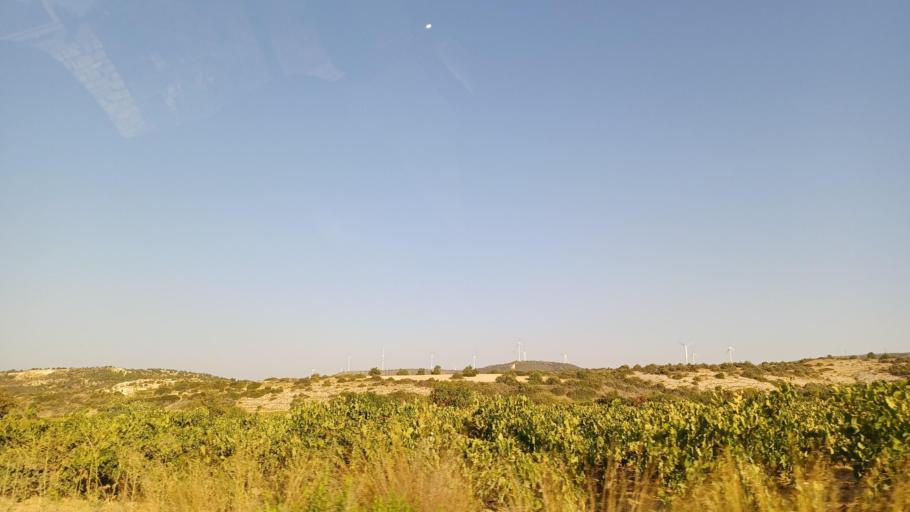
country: CY
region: Limassol
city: Pissouri
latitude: 34.7066
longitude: 32.6789
